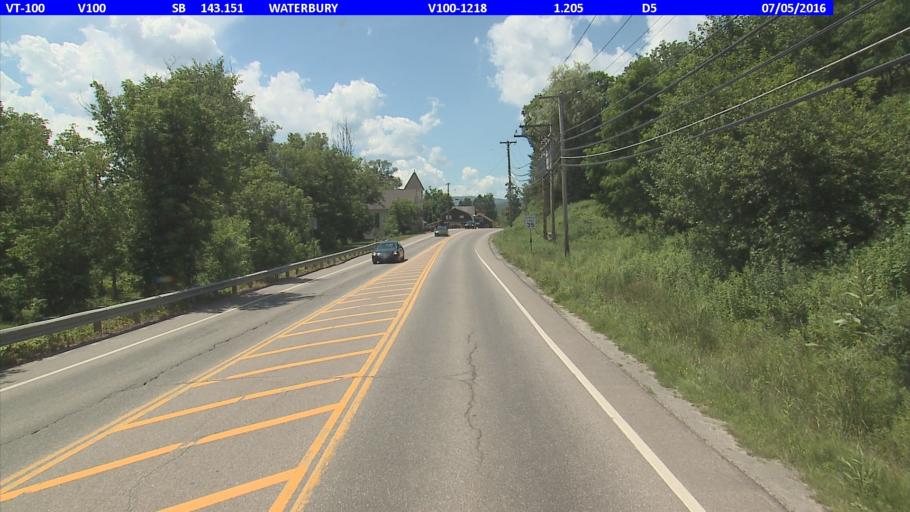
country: US
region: Vermont
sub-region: Washington County
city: Waterbury
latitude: 44.3511
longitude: -72.7406
